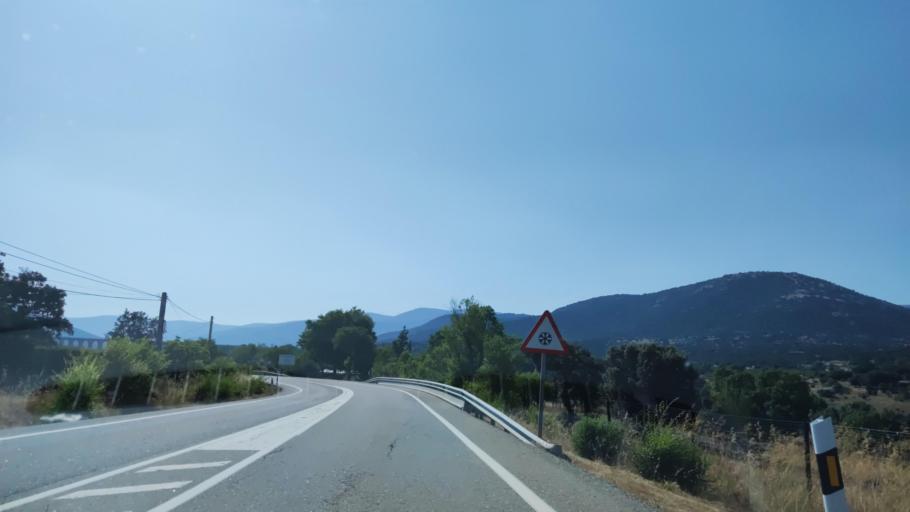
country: ES
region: Madrid
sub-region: Provincia de Madrid
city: Garganta de los Montes
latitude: 40.9436
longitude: -3.7111
